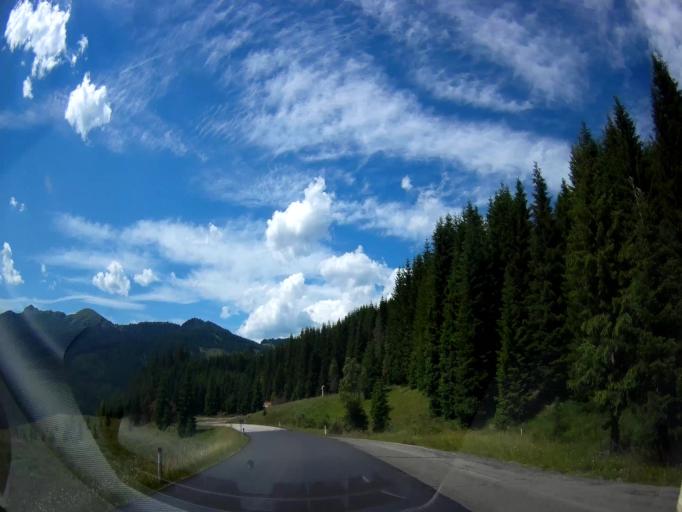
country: AT
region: Styria
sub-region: Politischer Bezirk Murau
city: Stadl an der Mur
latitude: 46.9709
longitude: 14.0161
